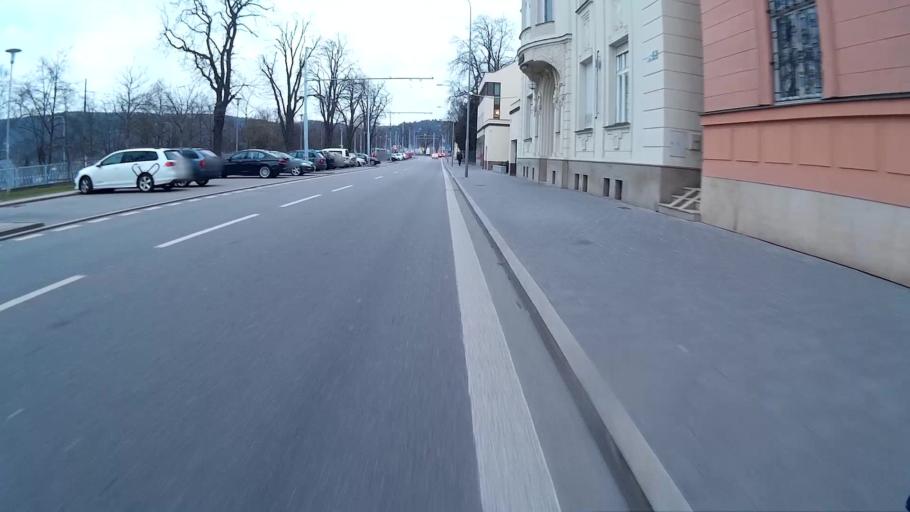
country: CZ
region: South Moravian
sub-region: Mesto Brno
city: Brno
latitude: 49.1911
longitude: 16.5782
